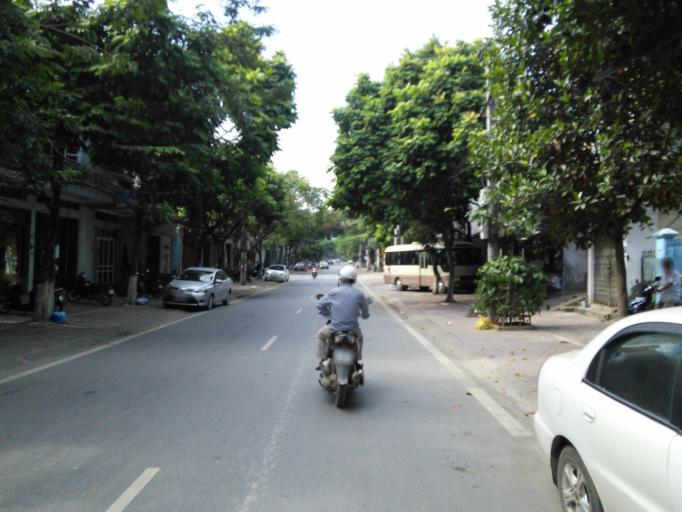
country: VN
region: Lao Cai
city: Lao Cai
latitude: 22.4840
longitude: 103.9771
